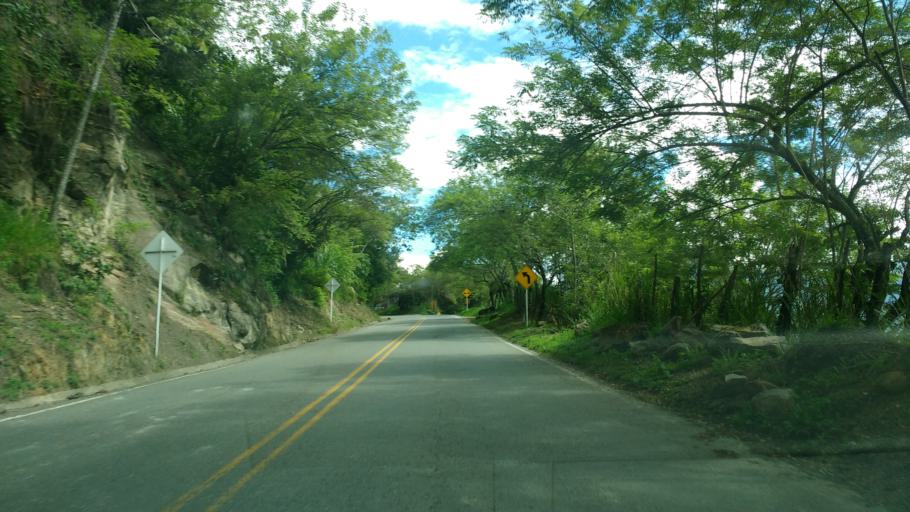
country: CO
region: Antioquia
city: Titiribi
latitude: 6.0246
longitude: -75.7660
